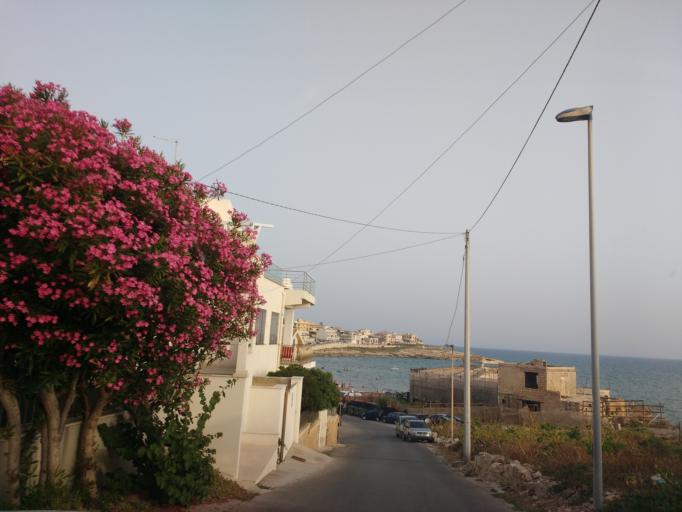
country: IT
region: Sicily
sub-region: Ragusa
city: Cava d'Aliga
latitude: 36.7297
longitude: 14.6837
